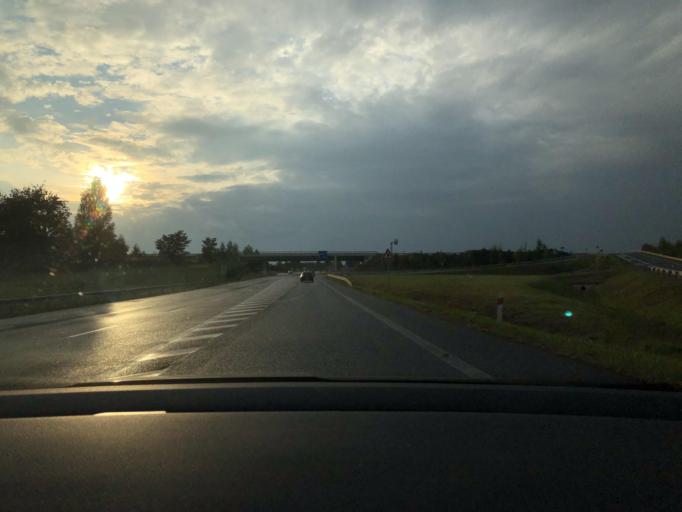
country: CZ
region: Central Bohemia
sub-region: Okres Kolin
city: Kolin
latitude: 50.0332
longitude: 15.1727
